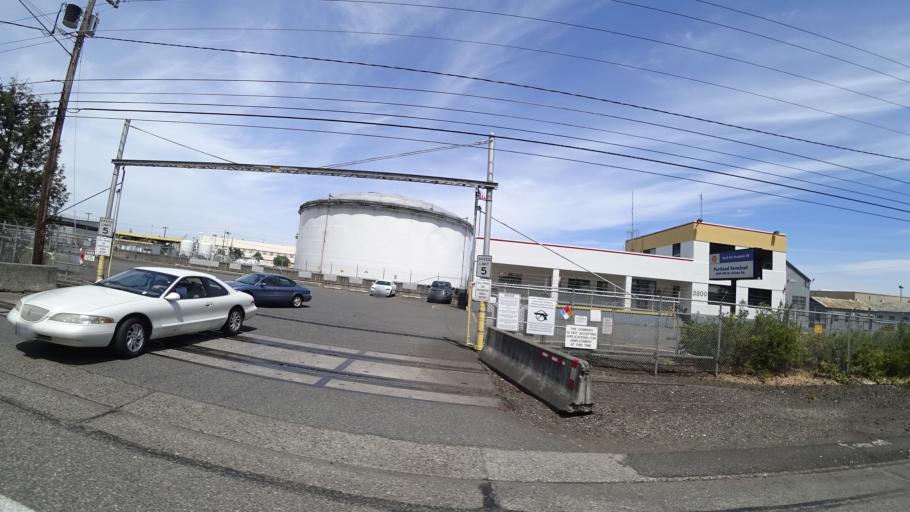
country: US
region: Oregon
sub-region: Washington County
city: West Haven-Sylvan
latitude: 45.5496
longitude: -122.7276
